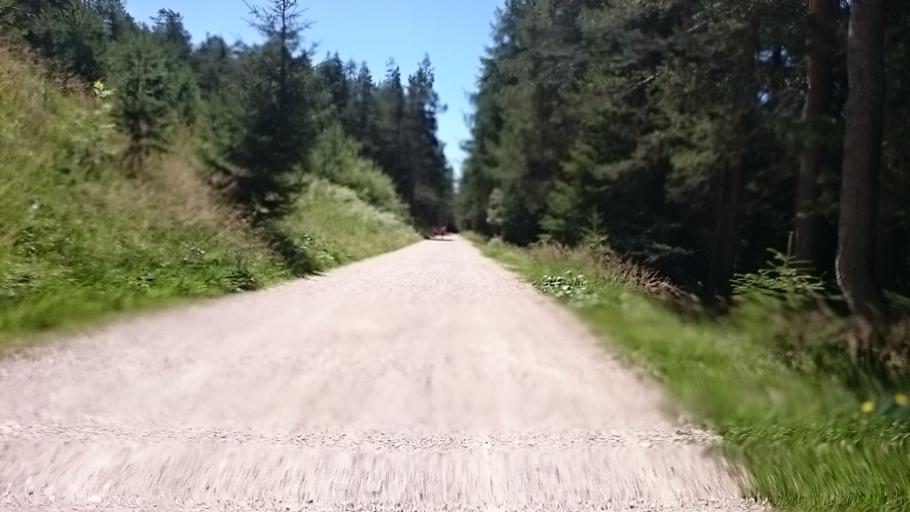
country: IT
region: Veneto
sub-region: Provincia di Belluno
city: Cortina d'Ampezzo
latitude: 46.5641
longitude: 12.1244
